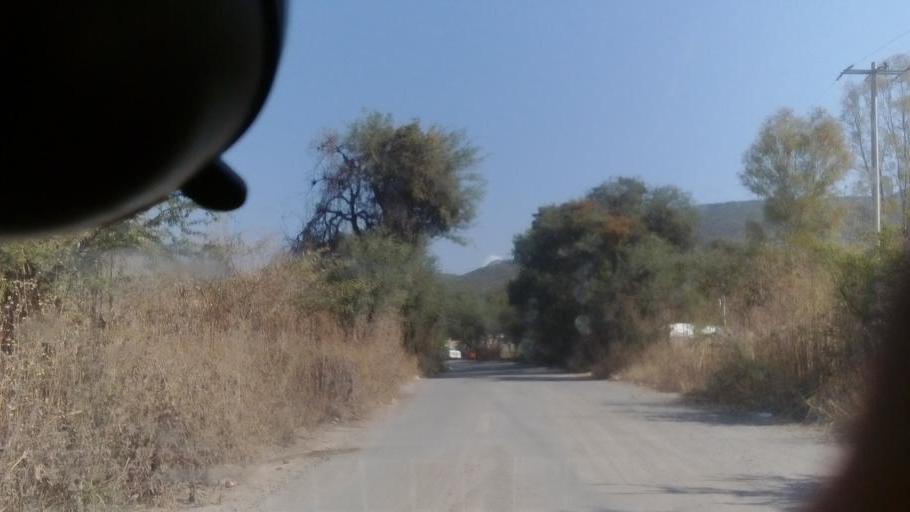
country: MX
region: Guanajuato
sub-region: Leon
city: Medina
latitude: 21.1389
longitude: -101.6106
